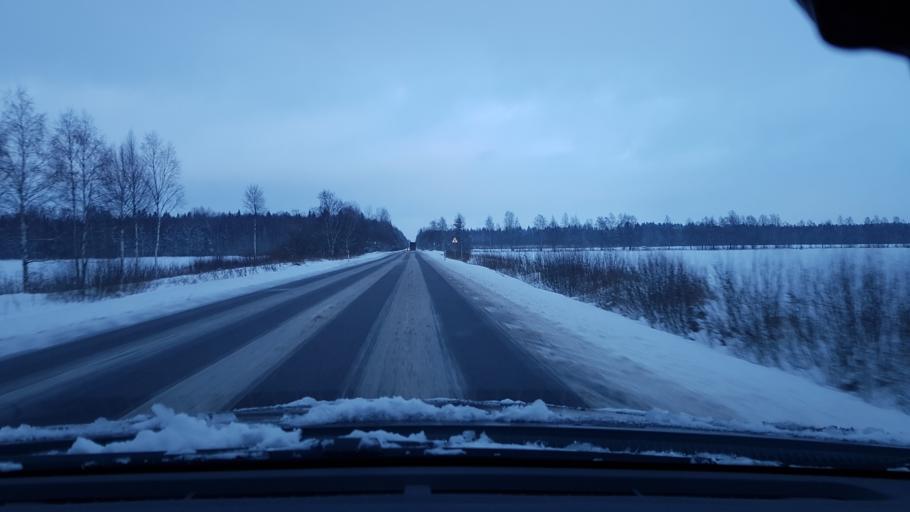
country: EE
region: Raplamaa
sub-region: Rapla vald
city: Rapla
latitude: 58.9501
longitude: 24.6287
